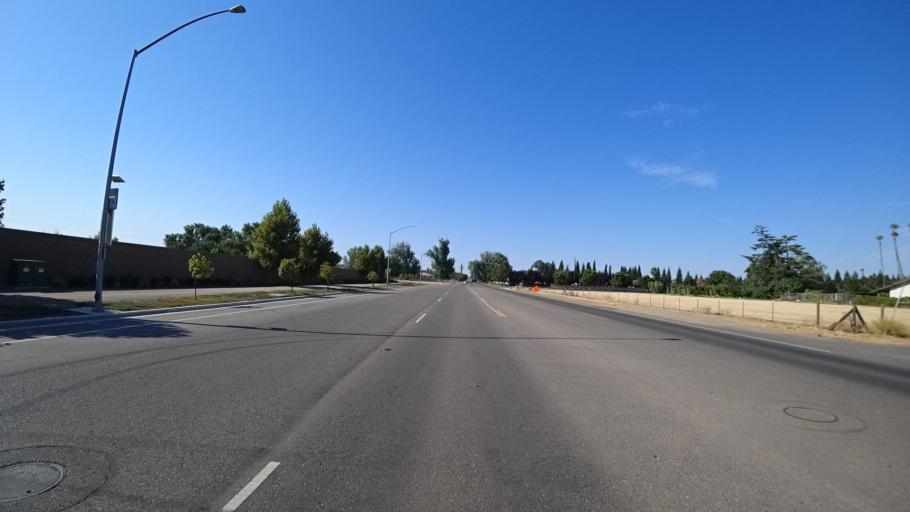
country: US
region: California
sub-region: Fresno County
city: Sunnyside
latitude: 36.7695
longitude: -119.6641
